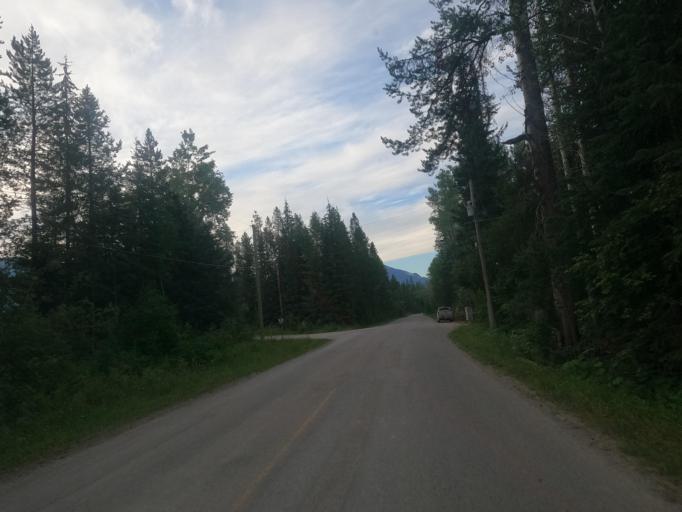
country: CA
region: British Columbia
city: Golden
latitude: 51.4314
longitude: -117.0470
